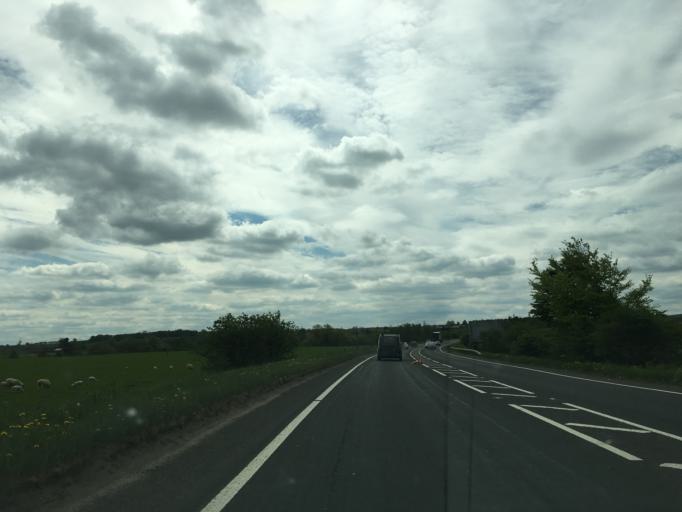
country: GB
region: Scotland
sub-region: Stirling
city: Bannockburn
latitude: 56.1049
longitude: -3.9052
